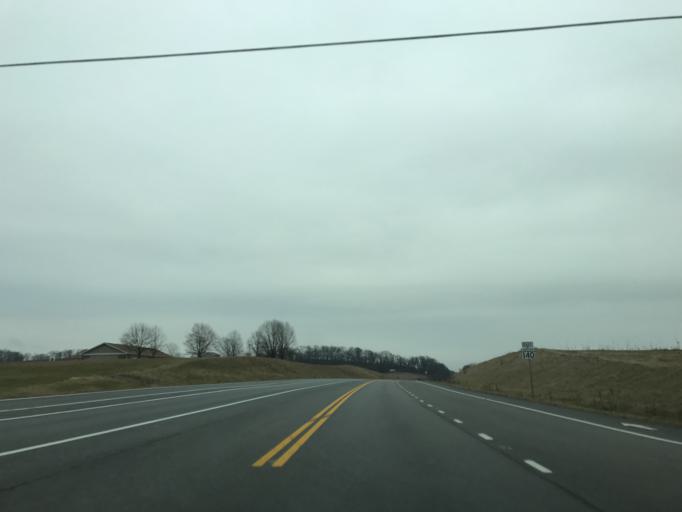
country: US
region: Maryland
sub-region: Carroll County
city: Westminster
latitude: 39.6071
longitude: -77.0630
